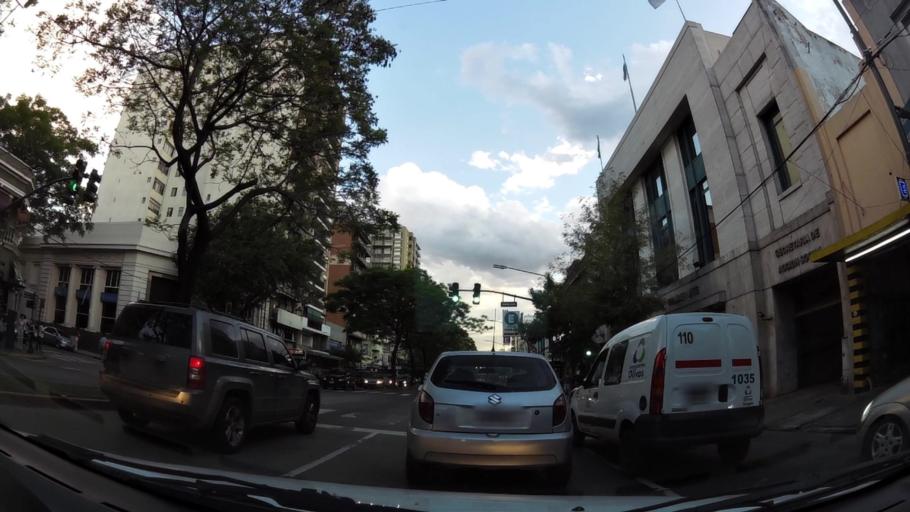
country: AR
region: Buenos Aires
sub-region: Partido de Vicente Lopez
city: Olivos
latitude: -34.5121
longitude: -58.4900
